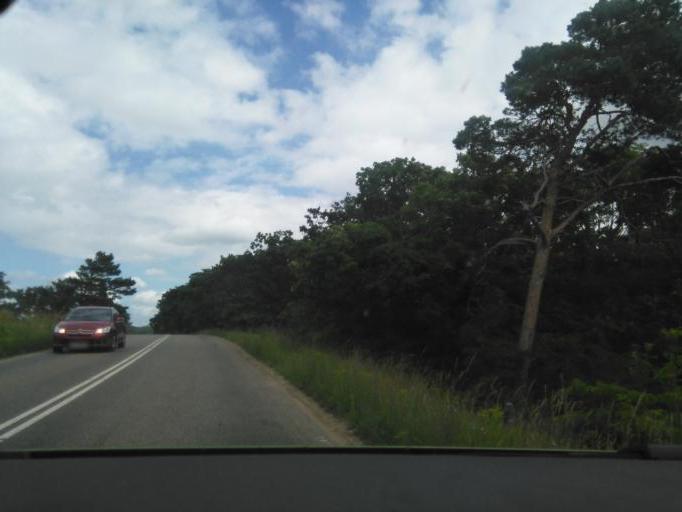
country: DK
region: Zealand
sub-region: Kalundborg Kommune
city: Hong
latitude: 55.5576
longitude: 11.3110
